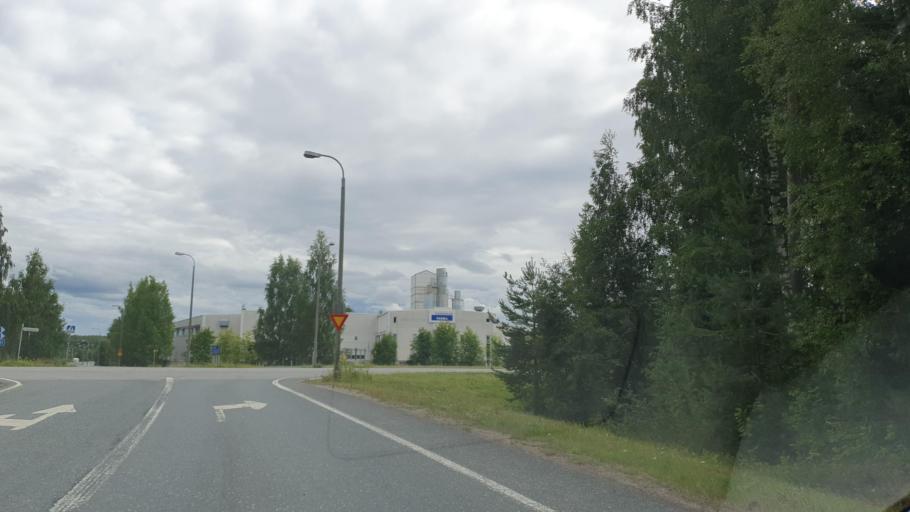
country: FI
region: Northern Savo
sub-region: Ylae-Savo
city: Iisalmi
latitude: 63.5248
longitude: 27.2465
